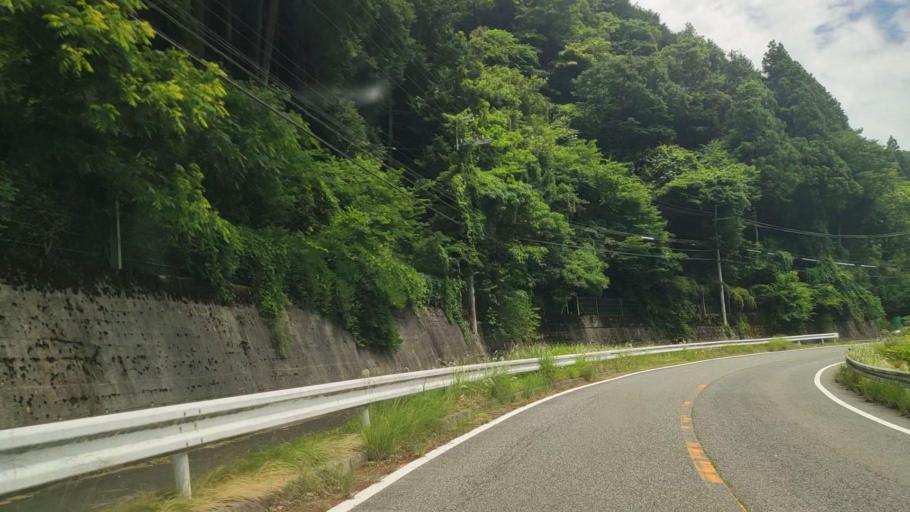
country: JP
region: Hyogo
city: Yamazakicho-nakabirose
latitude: 35.0933
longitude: 134.3624
